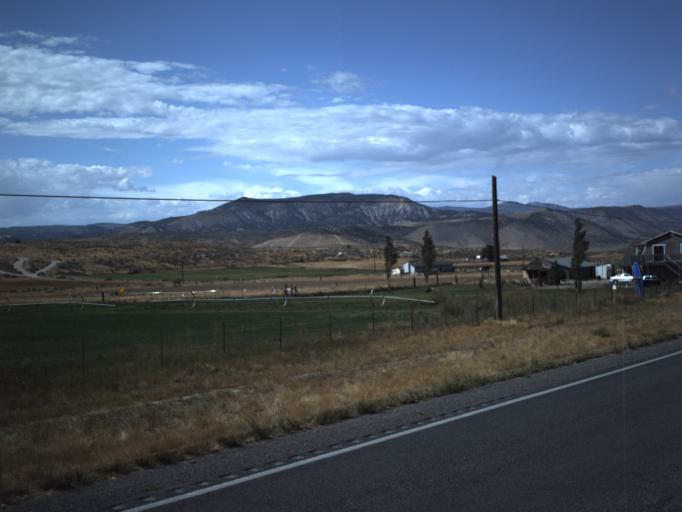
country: US
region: Utah
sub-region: Sanpete County
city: Manti
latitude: 39.2035
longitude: -111.6913
